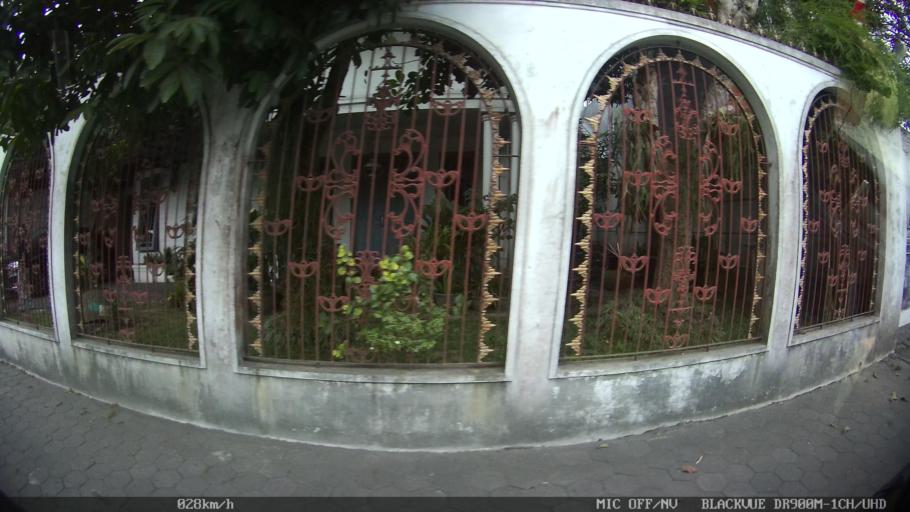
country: ID
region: Daerah Istimewa Yogyakarta
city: Gamping Lor
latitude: -7.7734
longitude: 110.3376
